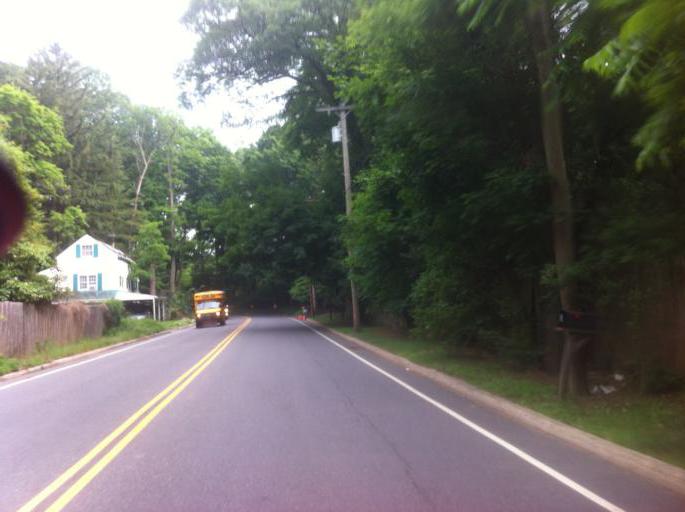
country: US
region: New York
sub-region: Nassau County
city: Locust Valley
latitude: 40.8735
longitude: -73.5745
